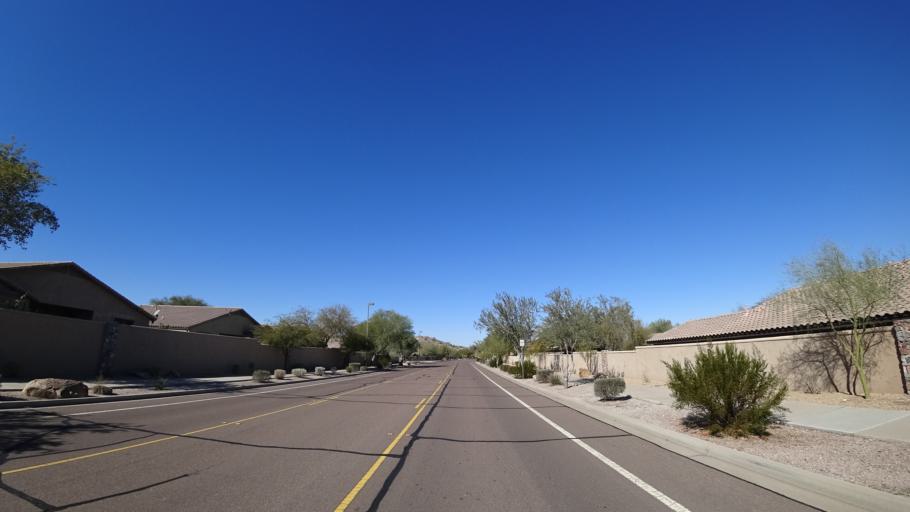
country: US
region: Arizona
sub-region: Maricopa County
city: Goodyear
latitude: 33.3544
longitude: -112.4457
